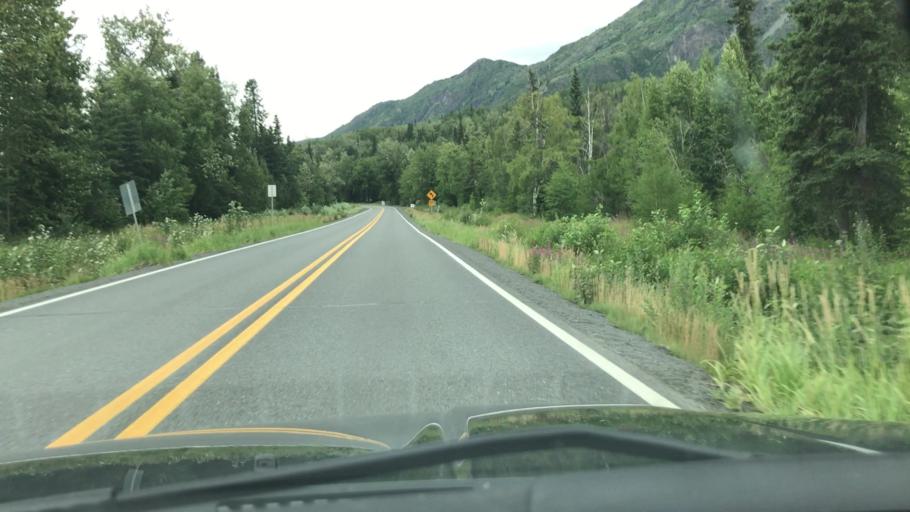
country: US
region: Alaska
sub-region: Kenai Peninsula Borough
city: Seward
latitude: 60.4875
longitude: -149.9732
